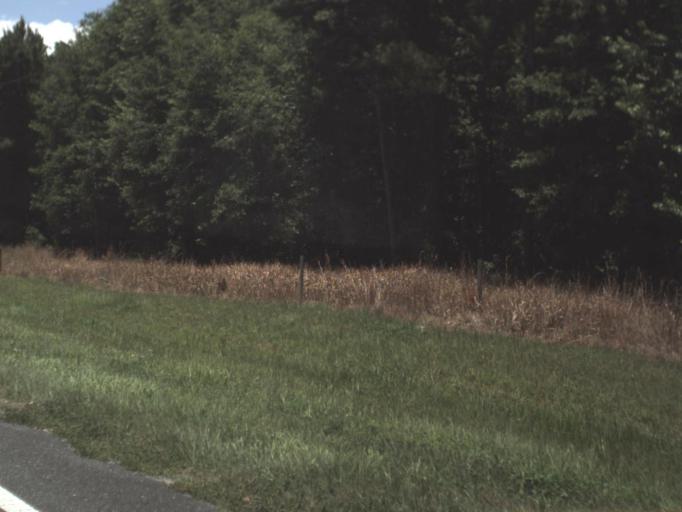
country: US
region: Florida
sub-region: Alachua County
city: Waldo
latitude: 29.7137
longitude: -82.1097
